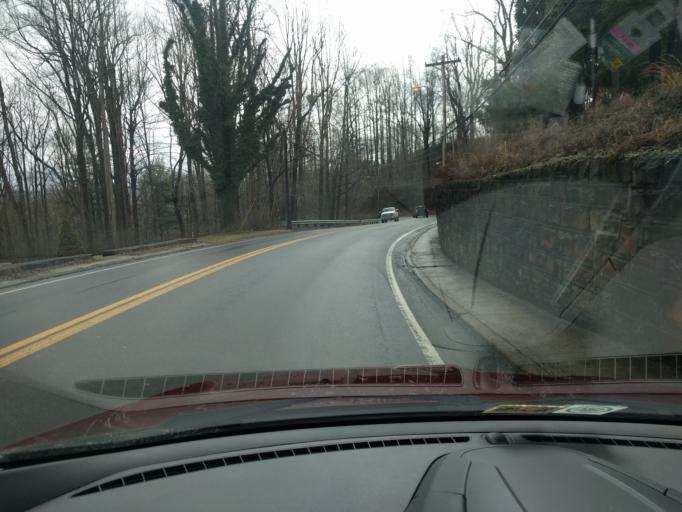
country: US
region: West Virginia
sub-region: Raleigh County
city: Mabscott
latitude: 37.7788
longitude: -81.2022
